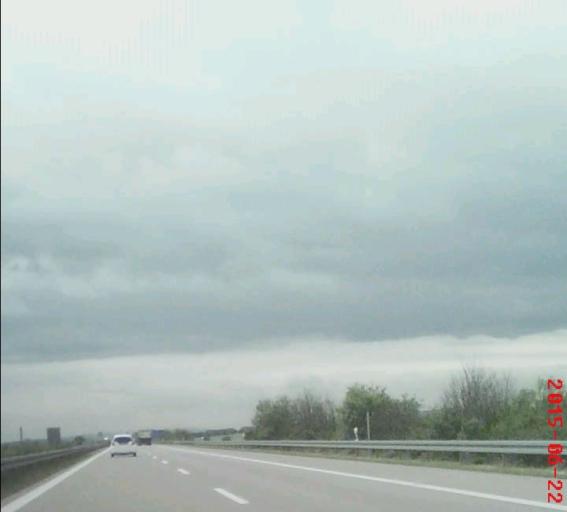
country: DE
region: Saxony-Anhalt
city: Farnstadt
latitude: 51.4433
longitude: 11.5388
